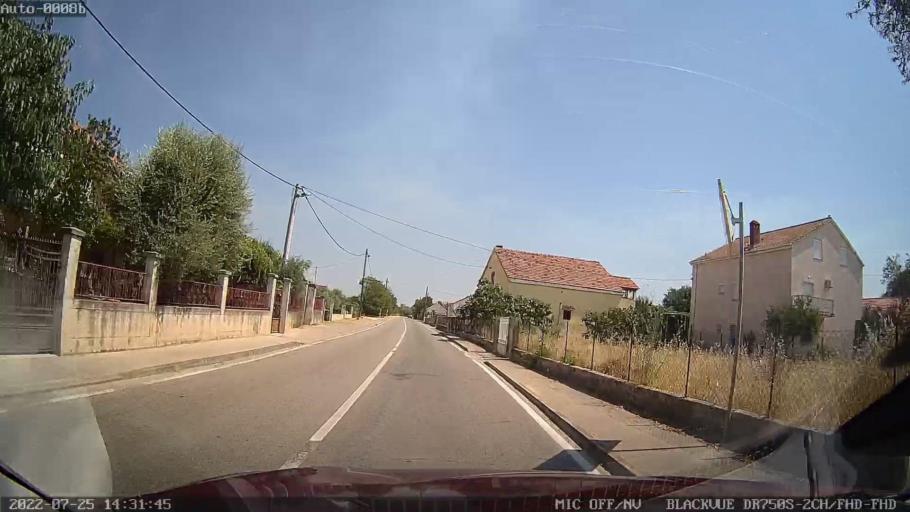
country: HR
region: Zadarska
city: Galovac
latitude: 44.1091
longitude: 15.3747
